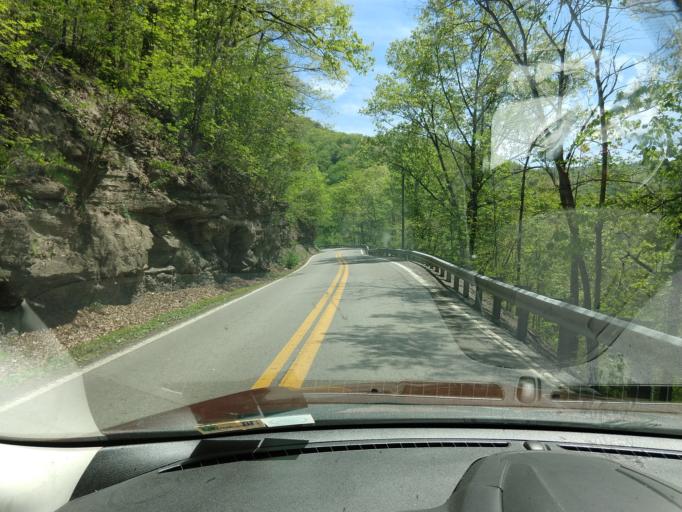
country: US
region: West Virginia
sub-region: McDowell County
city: Welch
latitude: 37.3138
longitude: -81.6964
